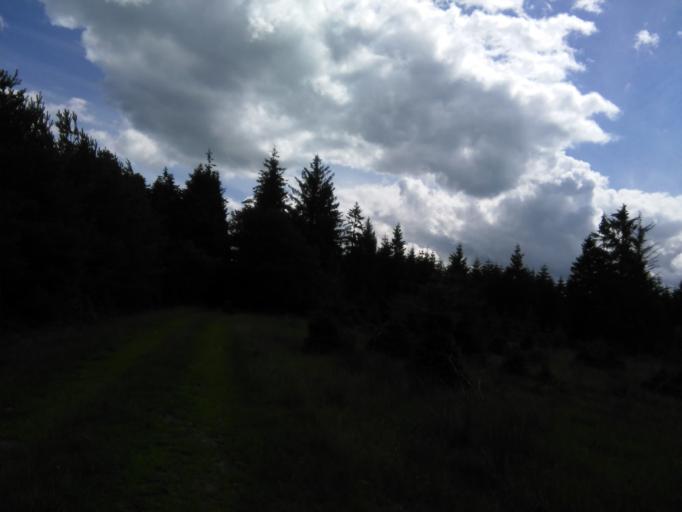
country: DK
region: Central Jutland
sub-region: Silkeborg Kommune
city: Virklund
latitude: 56.0826
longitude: 9.4273
